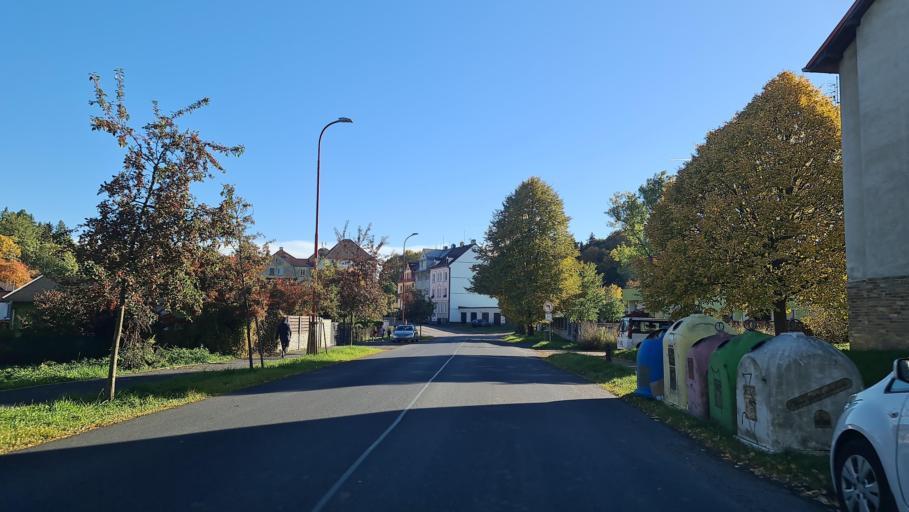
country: CZ
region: Karlovarsky
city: As
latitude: 50.2241
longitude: 12.1782
